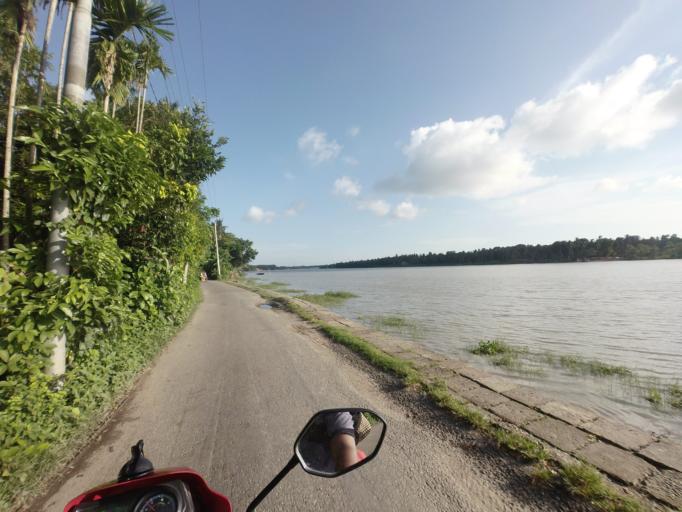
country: BD
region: Khulna
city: Khulna
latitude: 22.9106
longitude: 89.5199
